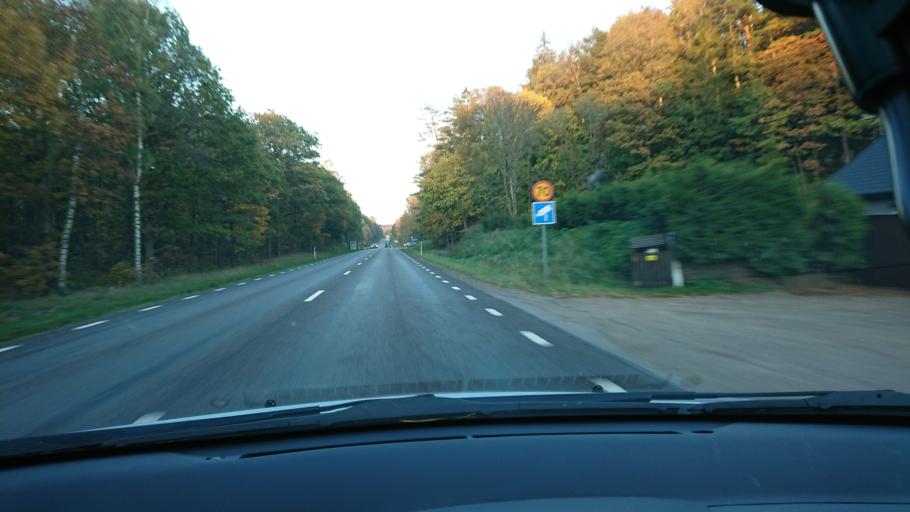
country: SE
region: Halland
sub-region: Halmstads Kommun
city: Aled
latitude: 56.7006
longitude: 13.0151
